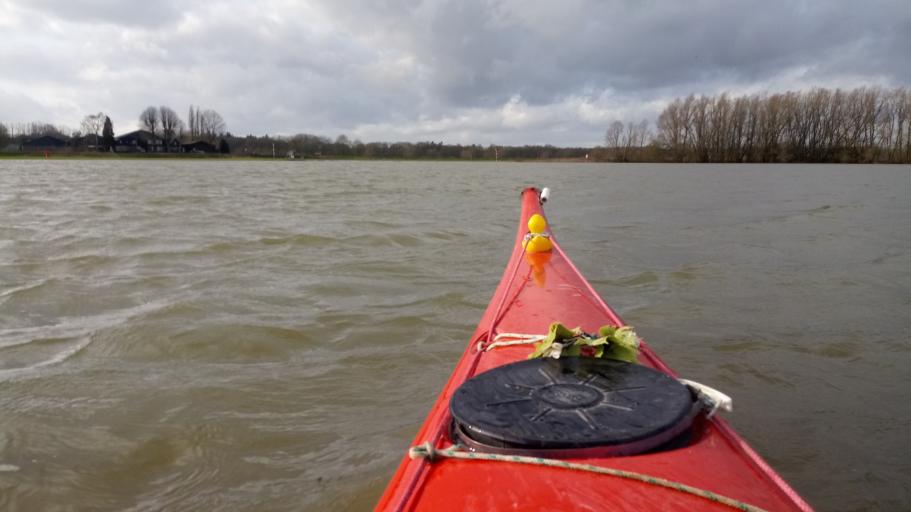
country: NL
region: Gelderland
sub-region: Gemeente Voorst
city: Wilp
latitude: 52.1921
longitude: 6.1604
